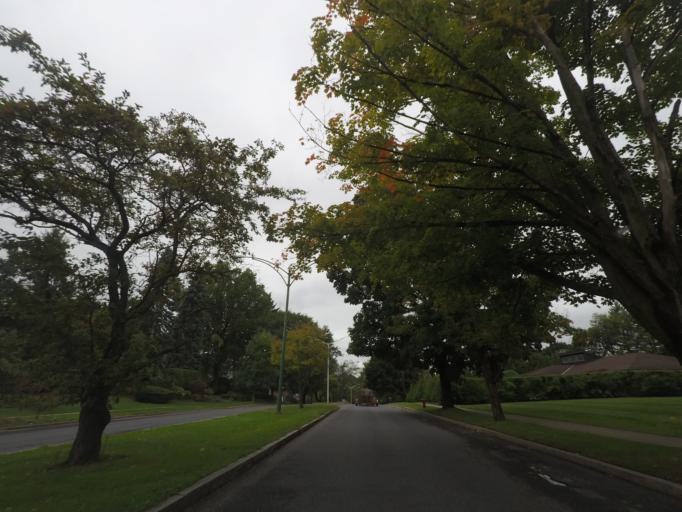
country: US
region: New York
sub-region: Albany County
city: West Albany
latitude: 42.6641
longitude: -73.7991
